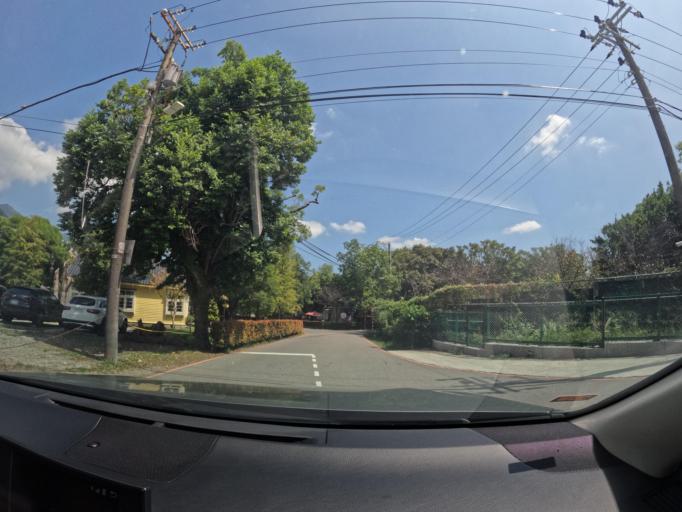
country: TW
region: Taipei
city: Taipei
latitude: 25.1365
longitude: 121.5417
